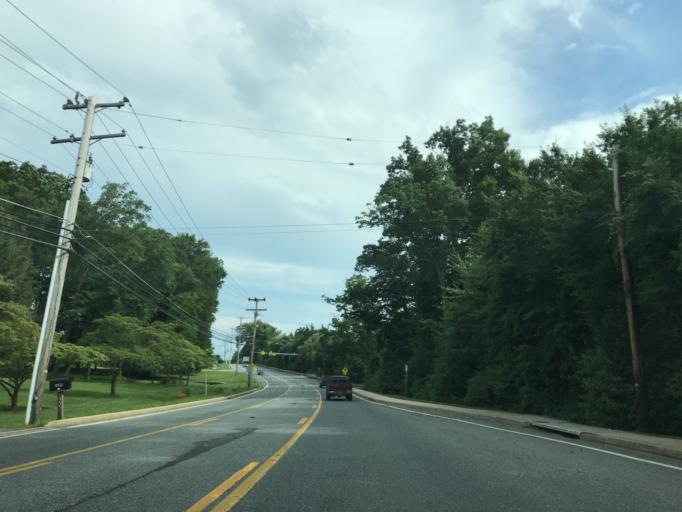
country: US
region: Maryland
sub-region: Harford County
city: South Bel Air
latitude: 39.5631
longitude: -76.3332
